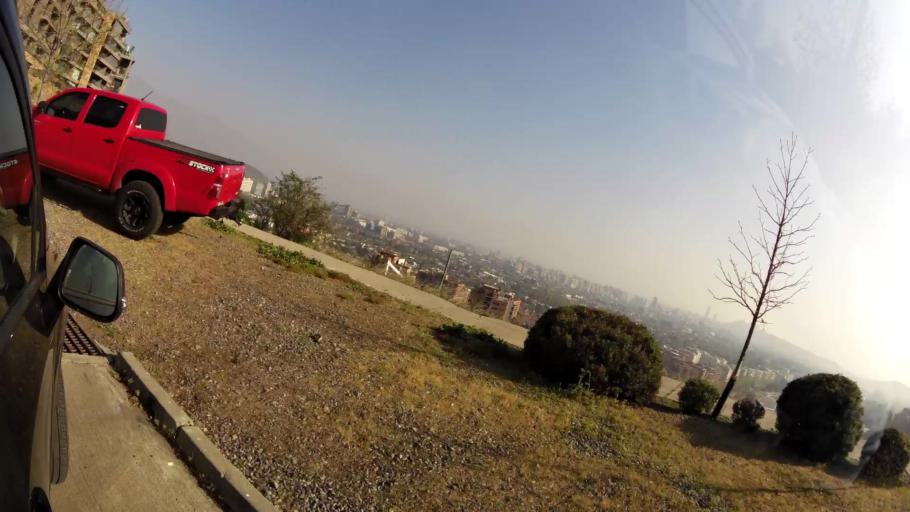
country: CL
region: Santiago Metropolitan
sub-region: Provincia de Santiago
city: Villa Presidente Frei, Nunoa, Santiago, Chile
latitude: -33.3721
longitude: -70.5441
